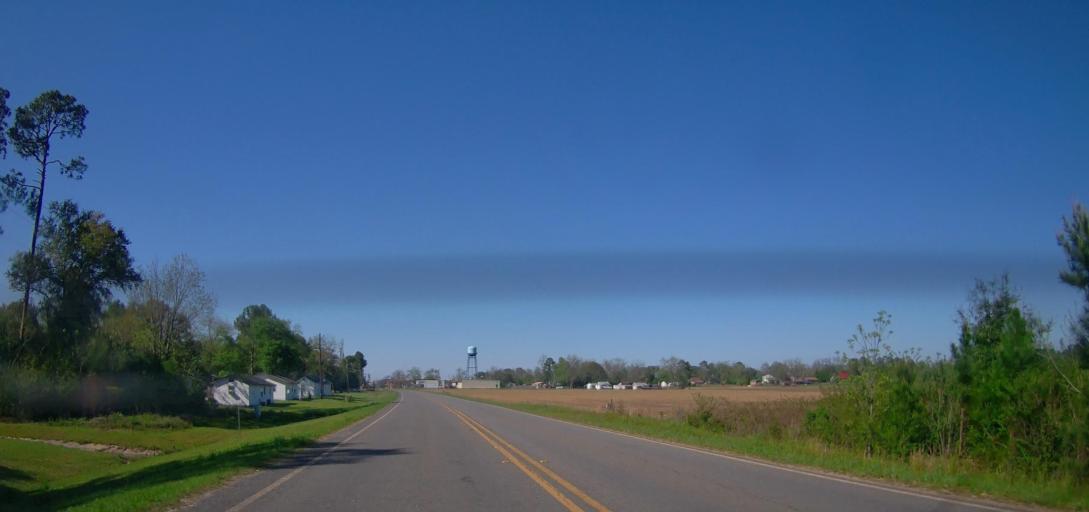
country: US
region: Georgia
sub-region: Wilcox County
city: Rochelle
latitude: 32.1054
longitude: -83.5014
